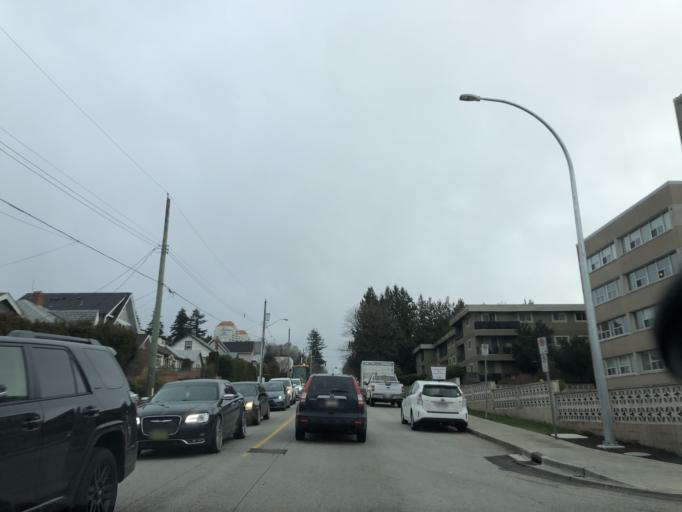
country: CA
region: British Columbia
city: New Westminster
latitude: 49.2083
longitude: -122.9293
